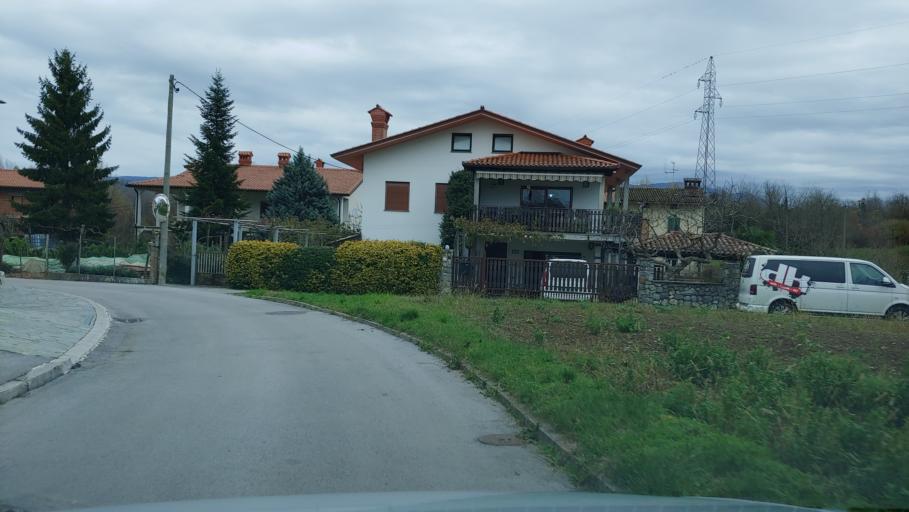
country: SI
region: Sempeter-Vrtojba
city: Vrtojba
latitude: 45.9071
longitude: 13.6370
